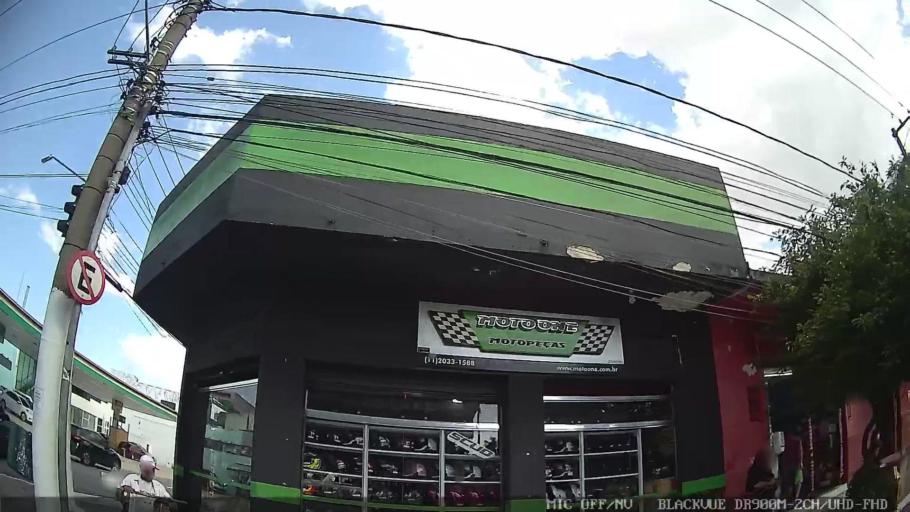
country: BR
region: Sao Paulo
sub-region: Ferraz De Vasconcelos
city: Ferraz de Vasconcelos
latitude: -23.4921
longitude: -46.4449
